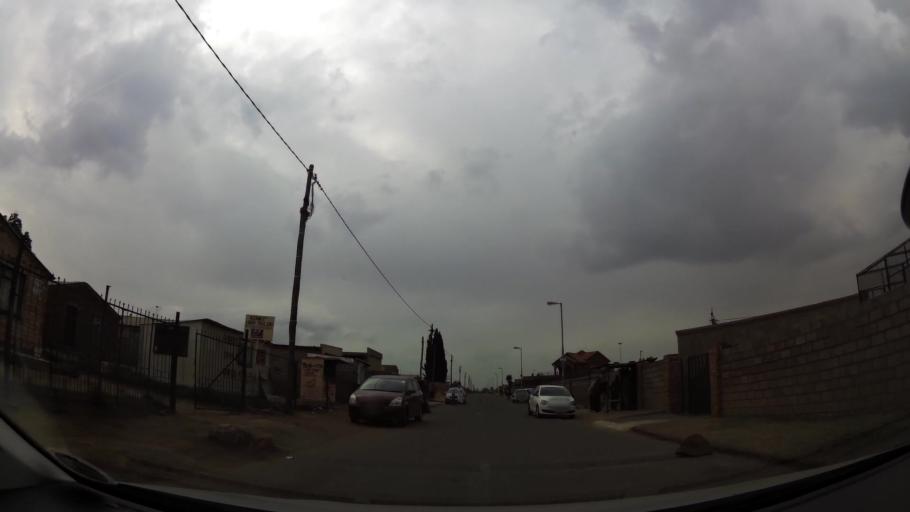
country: ZA
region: Gauteng
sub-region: City of Johannesburg Metropolitan Municipality
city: Soweto
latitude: -26.2623
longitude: 27.8646
